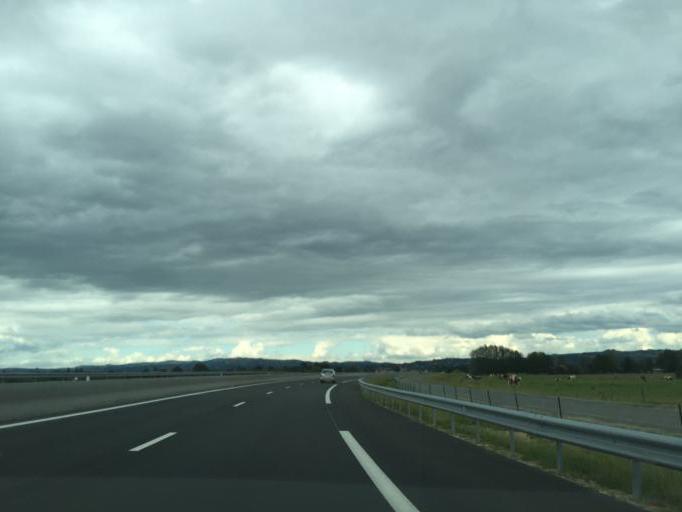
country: FR
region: Rhone-Alpes
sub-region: Departement de la Loire
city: Bonson
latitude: 45.5151
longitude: 4.2001
